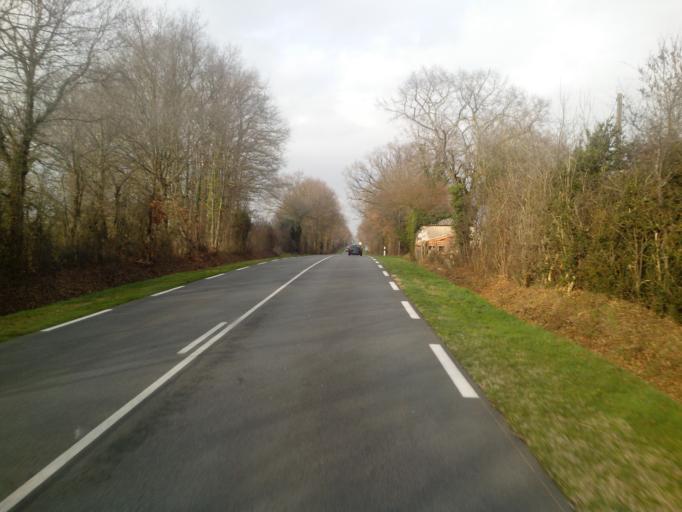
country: FR
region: Limousin
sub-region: Departement de la Haute-Vienne
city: Bussiere-Poitevine
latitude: 46.2772
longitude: 0.8577
